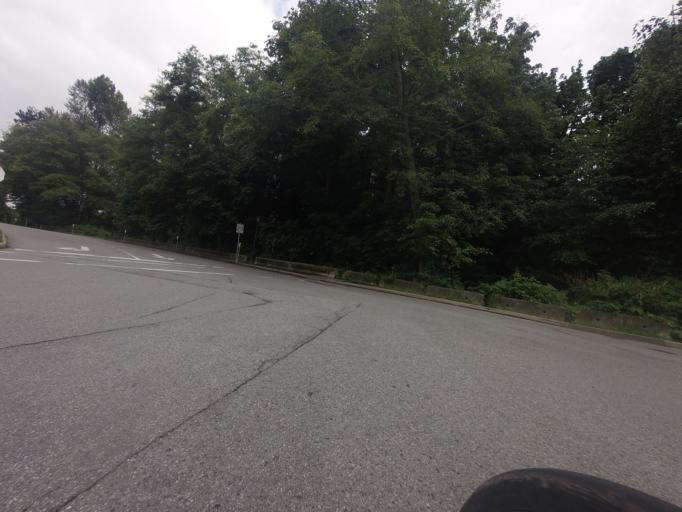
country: CA
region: British Columbia
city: West End
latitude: 49.3243
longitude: -123.1404
